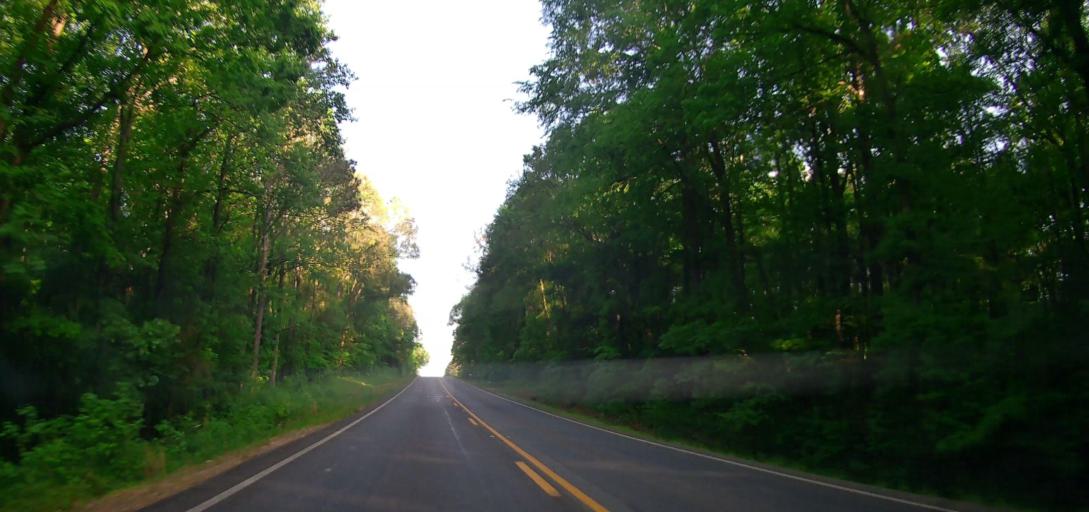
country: US
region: Georgia
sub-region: Putnam County
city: Eatonton
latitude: 33.3574
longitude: -83.5206
